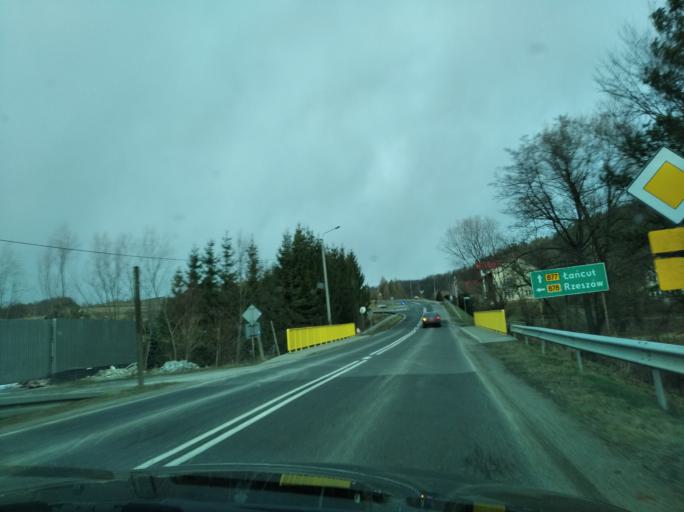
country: PL
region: Subcarpathian Voivodeship
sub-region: Powiat rzeszowski
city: Hyzne
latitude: 49.9099
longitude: 22.1994
